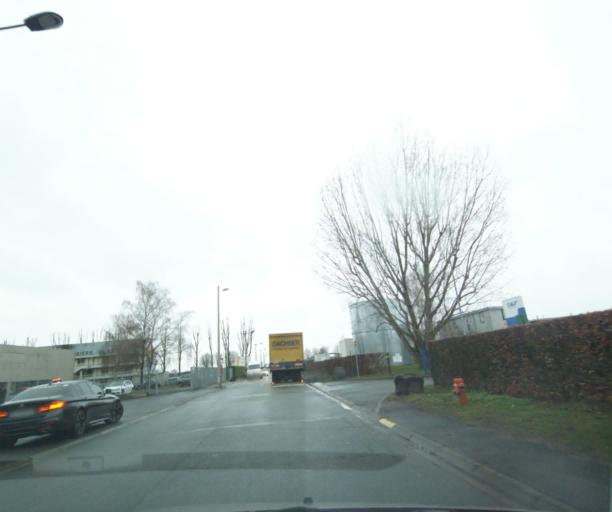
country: FR
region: Nord-Pas-de-Calais
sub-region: Departement du Nord
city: Prouvy
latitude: 50.3334
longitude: 3.4505
